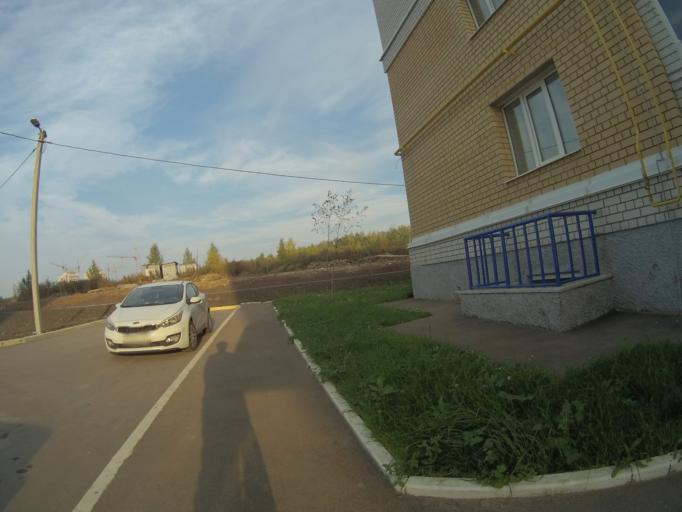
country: RU
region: Vladimir
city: Vladimir
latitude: 56.1610
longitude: 40.3734
